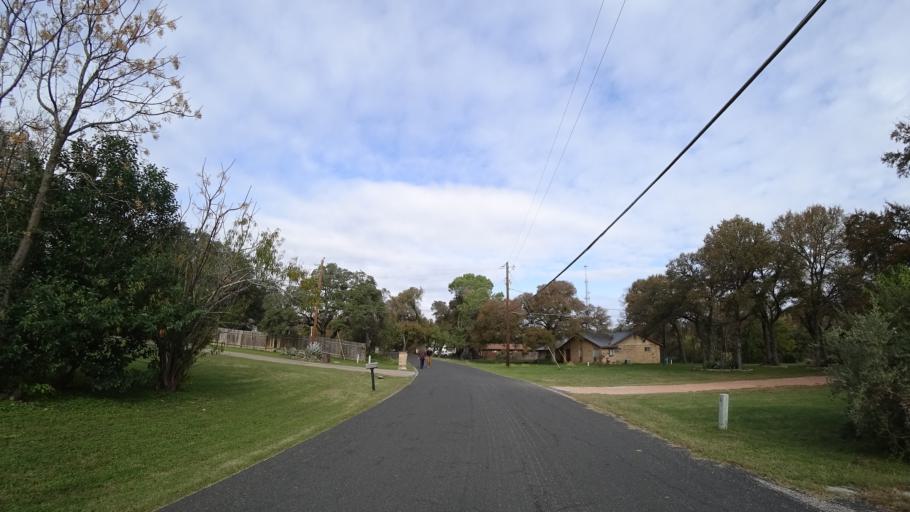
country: US
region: Texas
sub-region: Travis County
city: Manchaca
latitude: 30.1402
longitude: -97.8418
